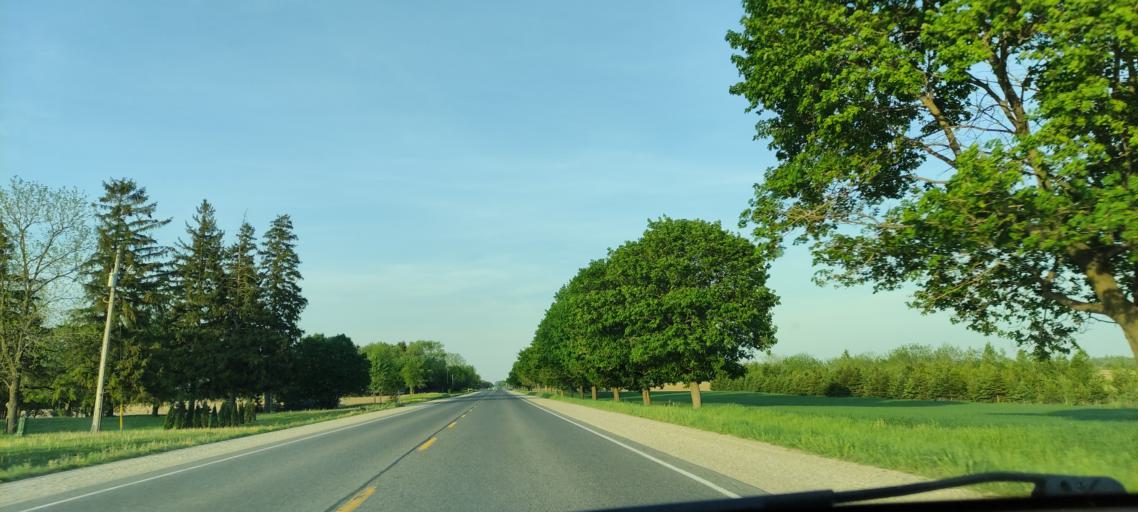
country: CA
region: Ontario
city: London
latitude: 43.1858
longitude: -81.2867
